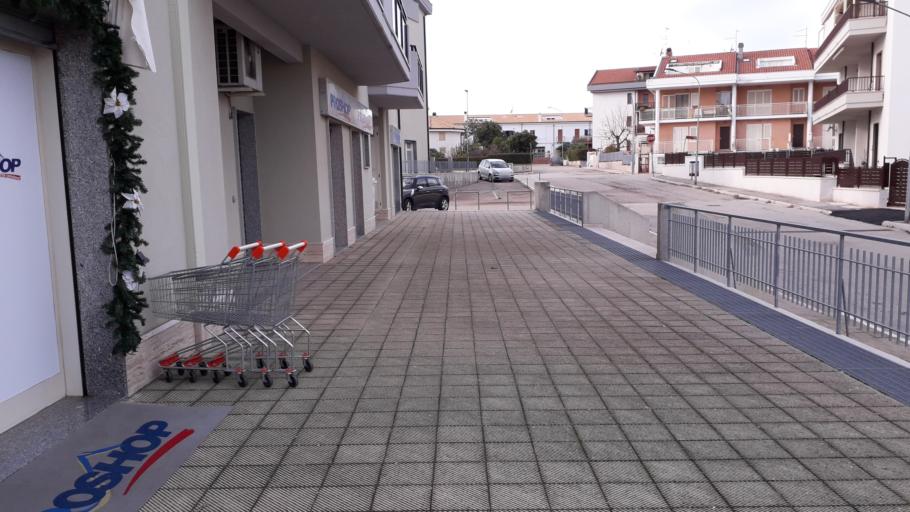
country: IT
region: Molise
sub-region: Provincia di Campobasso
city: Campomarino
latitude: 41.9534
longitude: 15.0351
